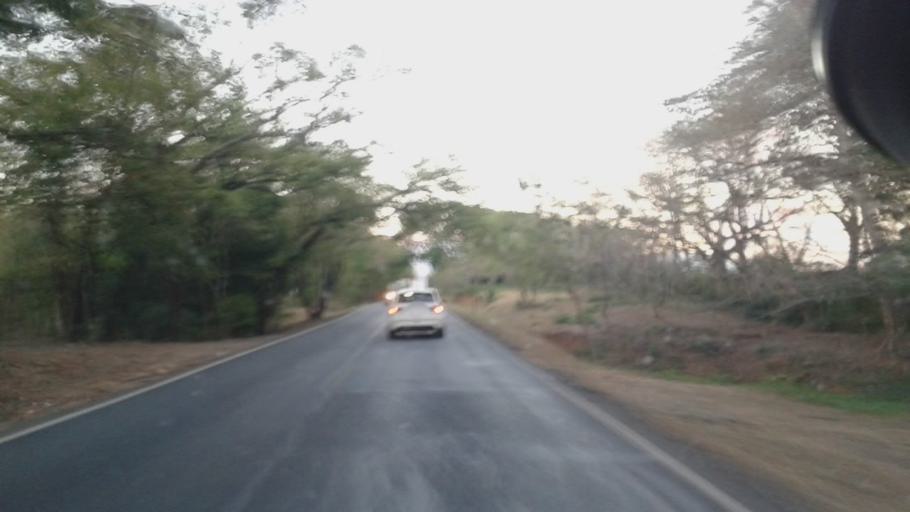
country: CR
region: Puntarenas
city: Miramar
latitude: 10.0917
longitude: -84.8259
